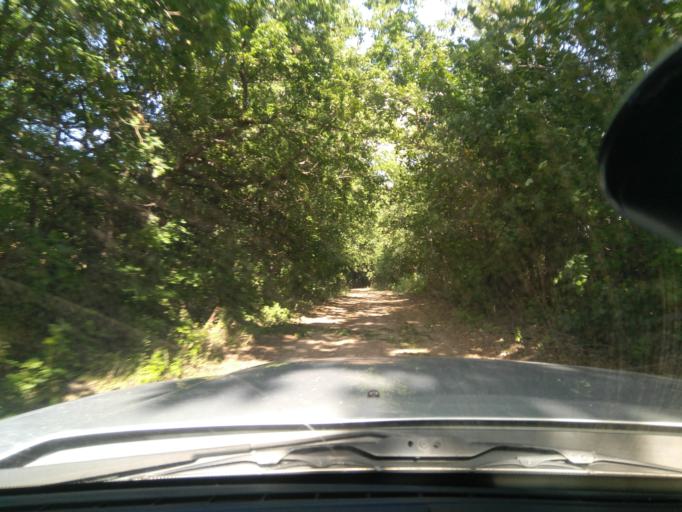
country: HU
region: Fejer
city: Bicske
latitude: 47.4413
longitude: 18.6482
